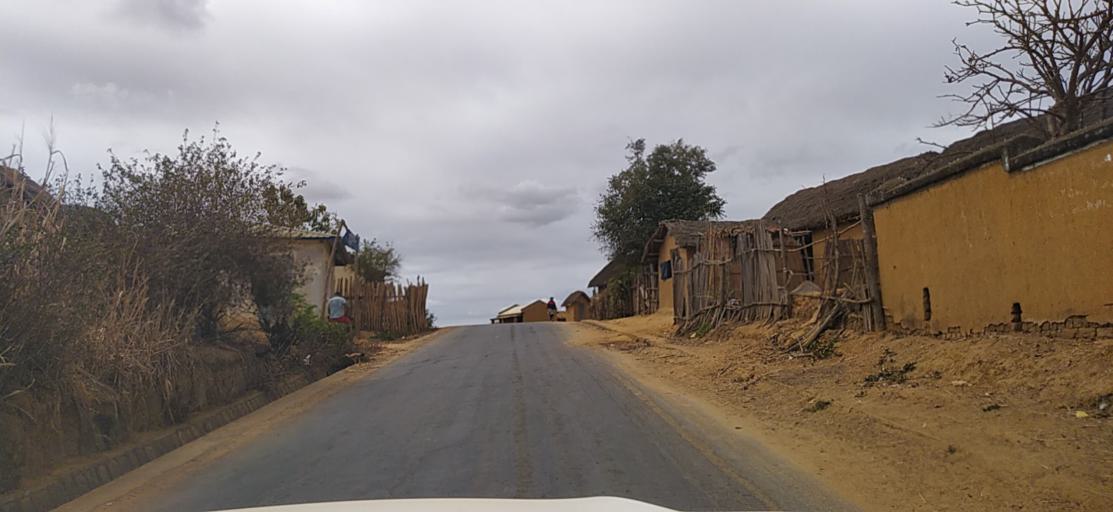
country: MG
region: Alaotra Mangoro
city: Ambatondrazaka
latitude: -17.9292
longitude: 48.2568
